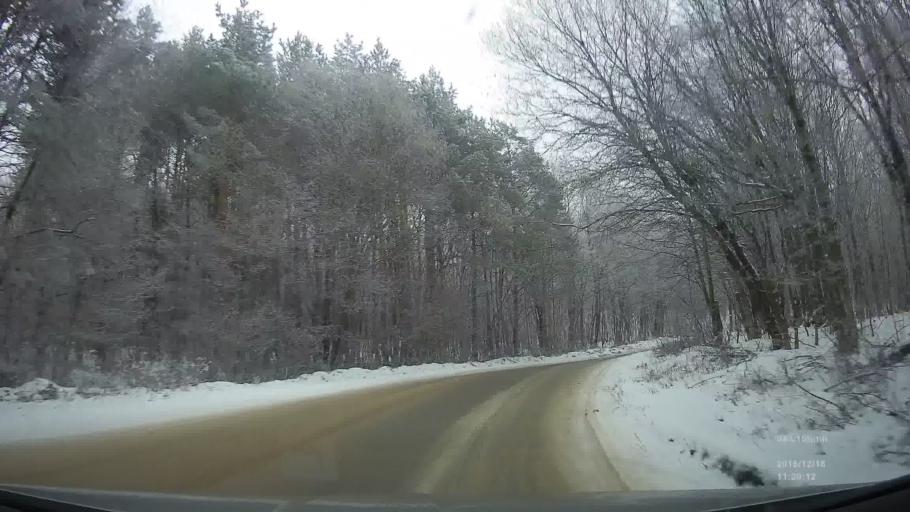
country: SK
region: Presovsky
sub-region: Okres Presov
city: Presov
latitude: 48.9112
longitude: 21.3585
